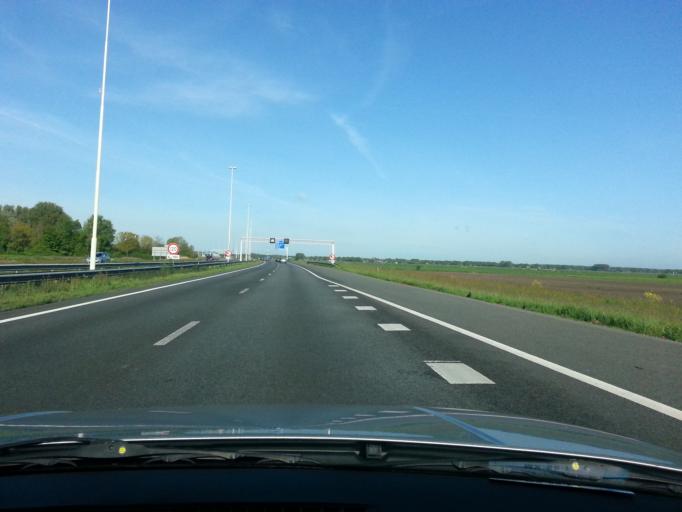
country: NL
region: Utrecht
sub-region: Gemeente Baarn
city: Baarn
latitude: 52.2218
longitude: 5.2945
